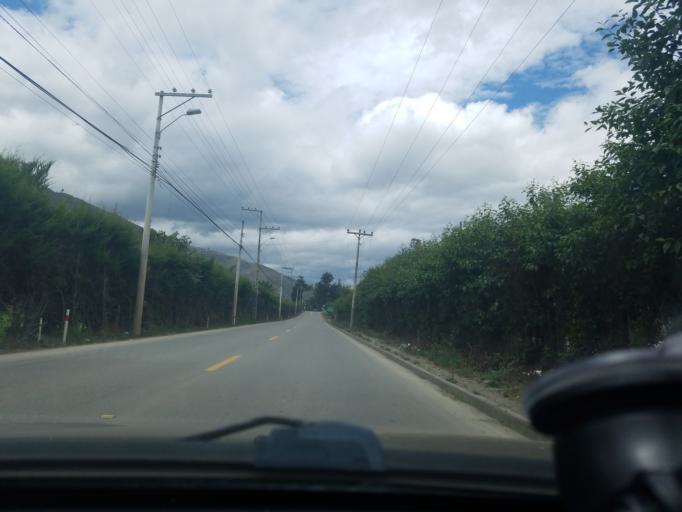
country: EC
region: Azuay
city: La Union
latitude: -2.8149
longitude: -78.7732
